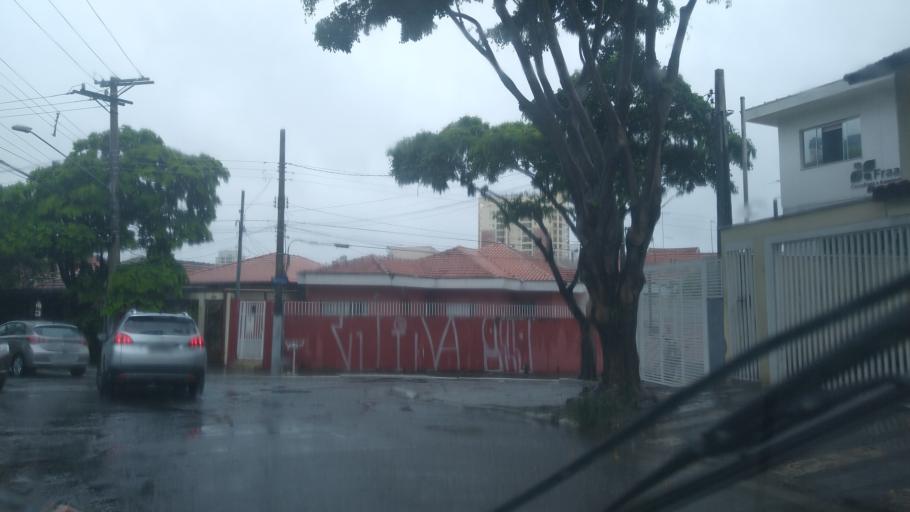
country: BR
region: Sao Paulo
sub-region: Sao Paulo
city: Sao Paulo
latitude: -23.4903
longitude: -46.6213
